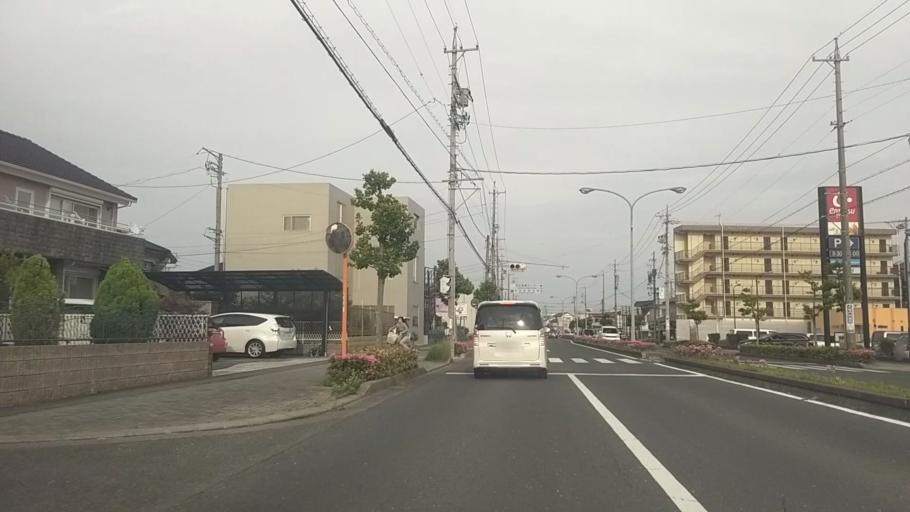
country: JP
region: Shizuoka
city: Hamamatsu
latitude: 34.7194
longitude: 137.7083
